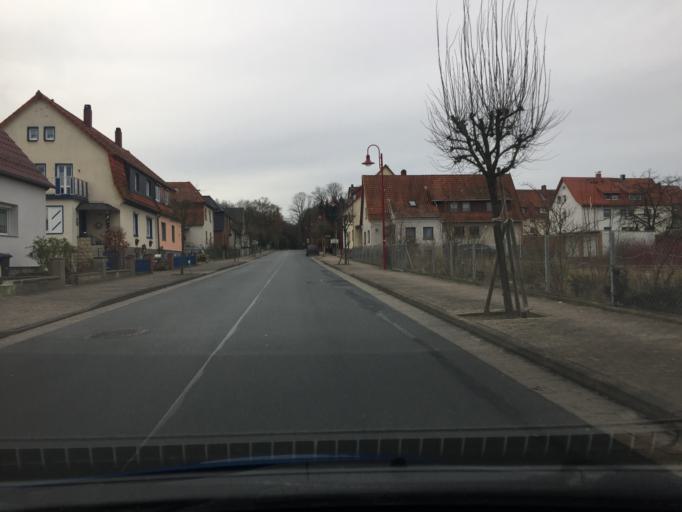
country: DE
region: Lower Saxony
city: Duingen
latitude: 52.0018
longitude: 9.6905
